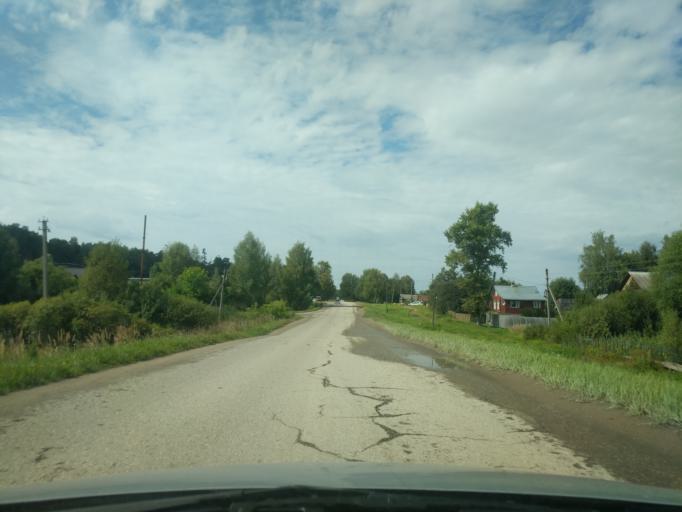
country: RU
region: Kostroma
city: Sudislavl'
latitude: 57.8789
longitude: 41.7237
